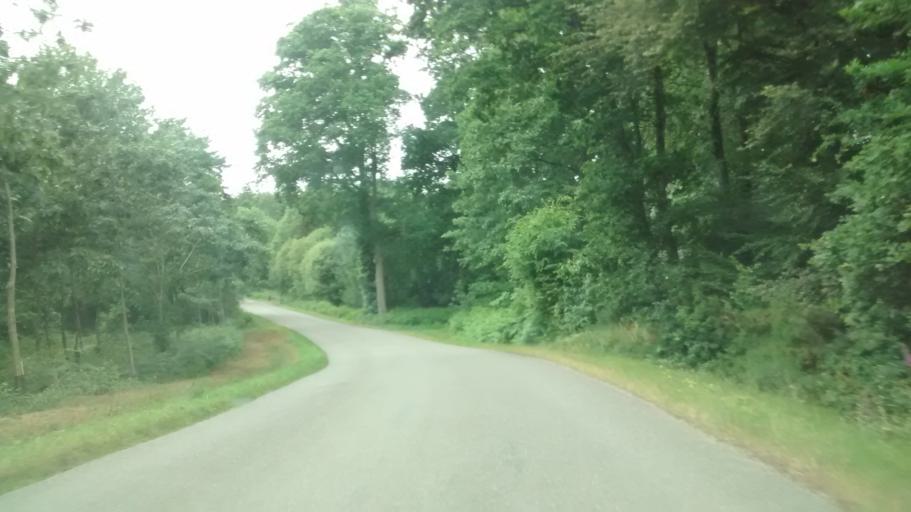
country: FR
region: Brittany
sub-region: Departement du Morbihan
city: Carentoir
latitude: 47.8332
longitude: -2.1933
